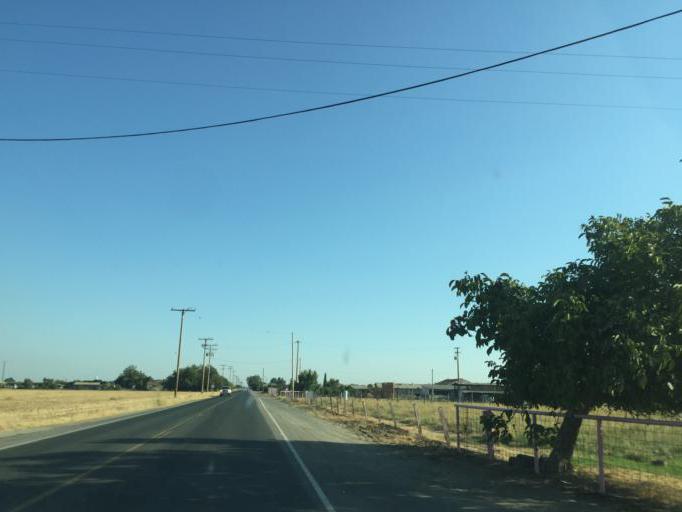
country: US
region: California
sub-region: Tulare County
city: Ivanhoe
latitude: 36.4395
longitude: -119.2778
